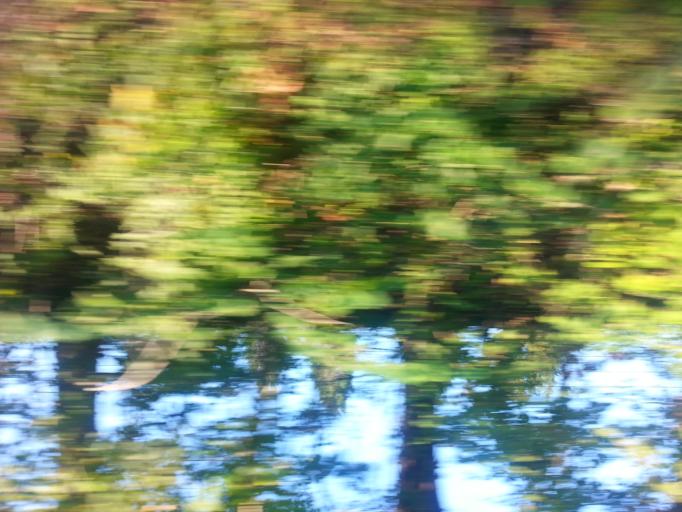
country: US
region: Tennessee
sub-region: Blount County
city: Wildwood
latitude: 35.8724
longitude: -83.8896
